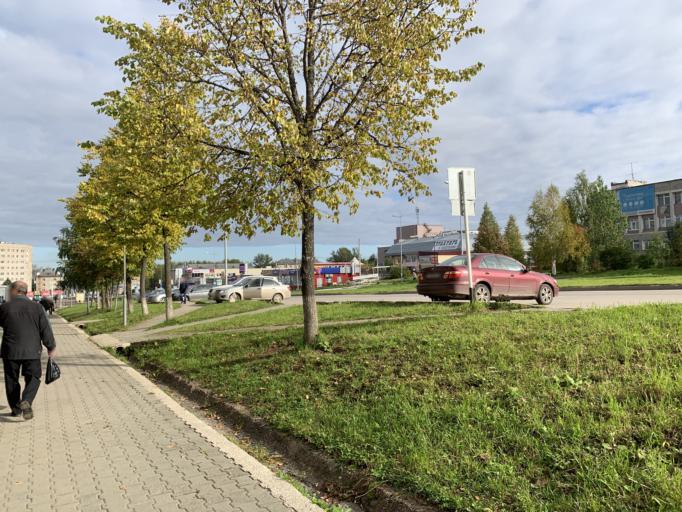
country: RU
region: Perm
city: Gubakha
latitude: 58.8348
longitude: 57.5556
